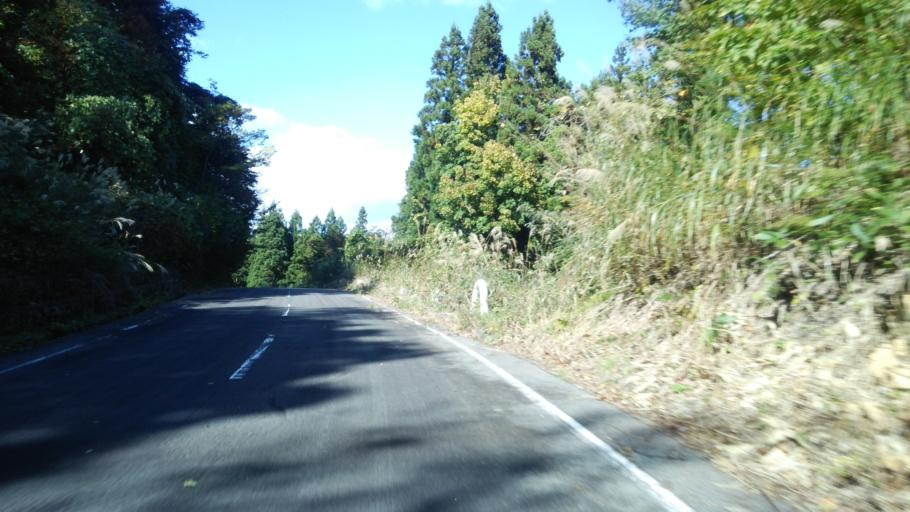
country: JP
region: Fukushima
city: Kitakata
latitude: 37.4359
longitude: 139.7804
